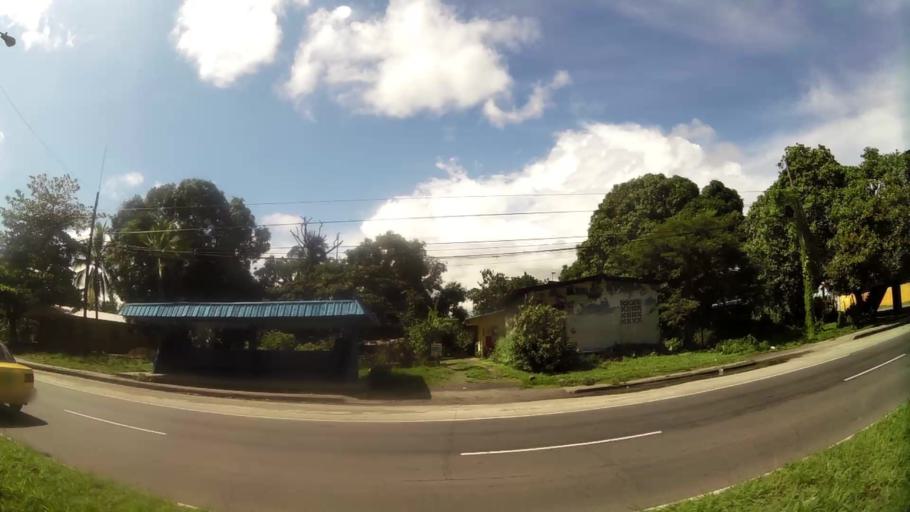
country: PA
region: Panama
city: Bejuco
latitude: 8.6080
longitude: -79.8850
